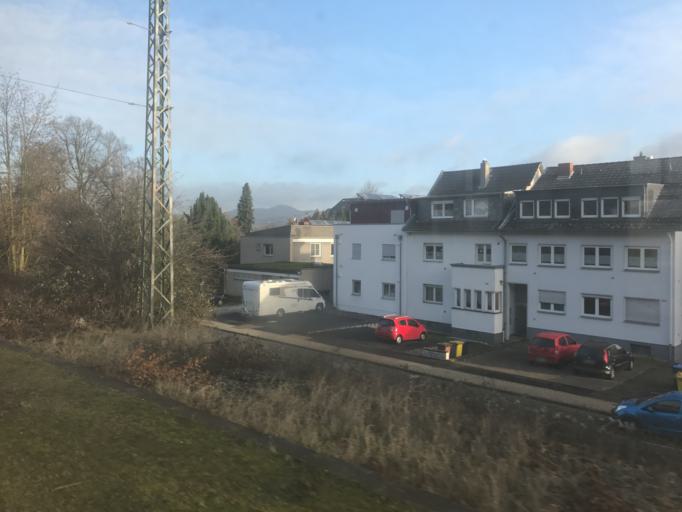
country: DE
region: Rheinland-Pfalz
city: Unkel
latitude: 50.6103
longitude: 7.2083
